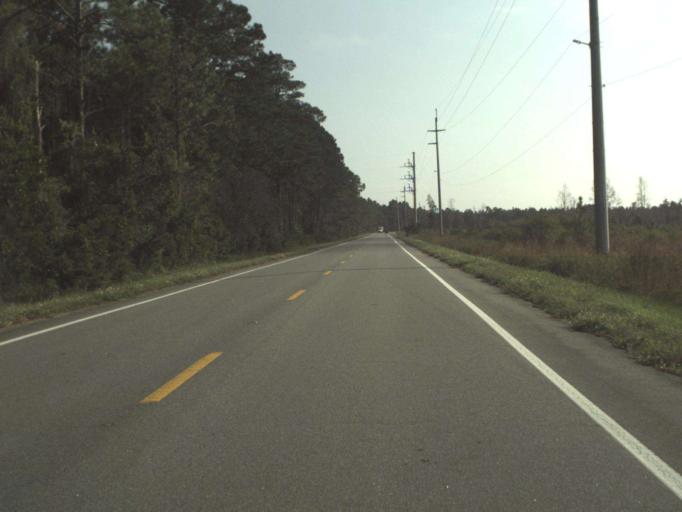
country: US
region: Florida
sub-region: Franklin County
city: Carrabelle
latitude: 29.9475
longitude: -84.5025
